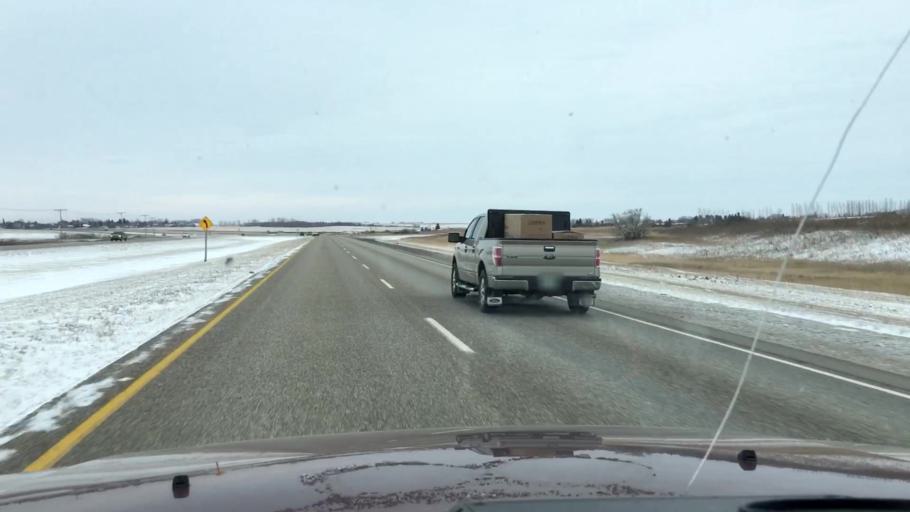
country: CA
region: Saskatchewan
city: Moose Jaw
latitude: 50.9526
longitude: -105.7089
